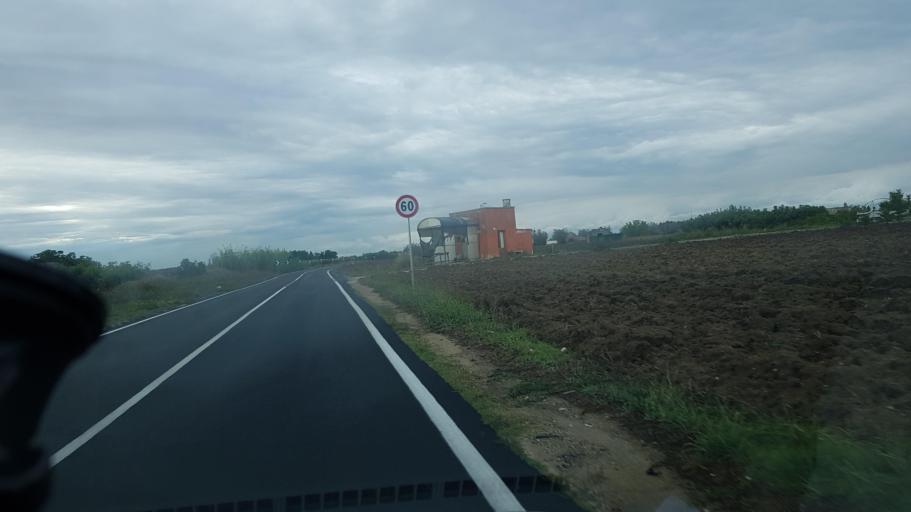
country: IT
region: Apulia
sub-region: Provincia di Lecce
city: Carmiano
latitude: 40.3591
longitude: 18.0168
